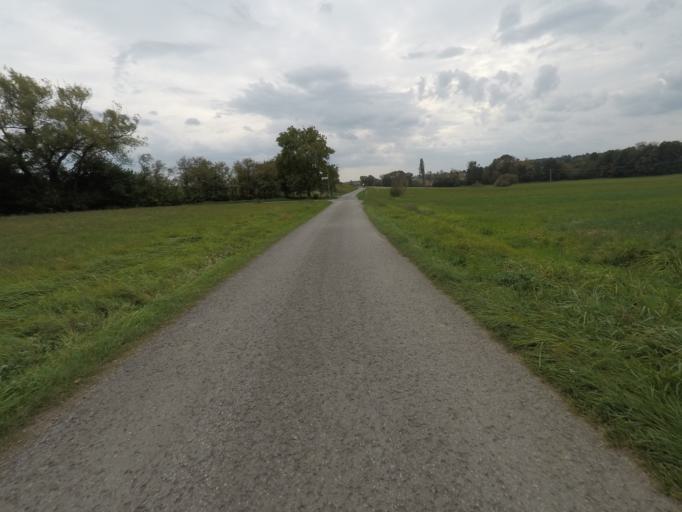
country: DE
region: Baden-Wuerttemberg
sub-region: Regierungsbezirk Stuttgart
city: Herrenberg
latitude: 48.5835
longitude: 8.8673
